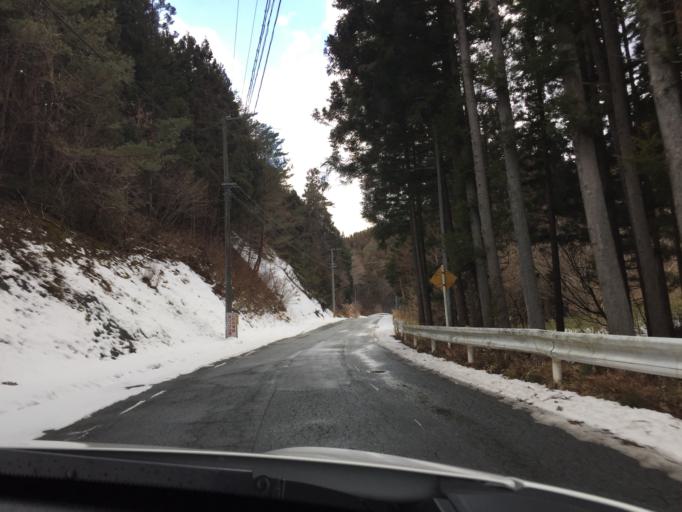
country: JP
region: Fukushima
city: Iwaki
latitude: 37.2233
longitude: 140.7442
